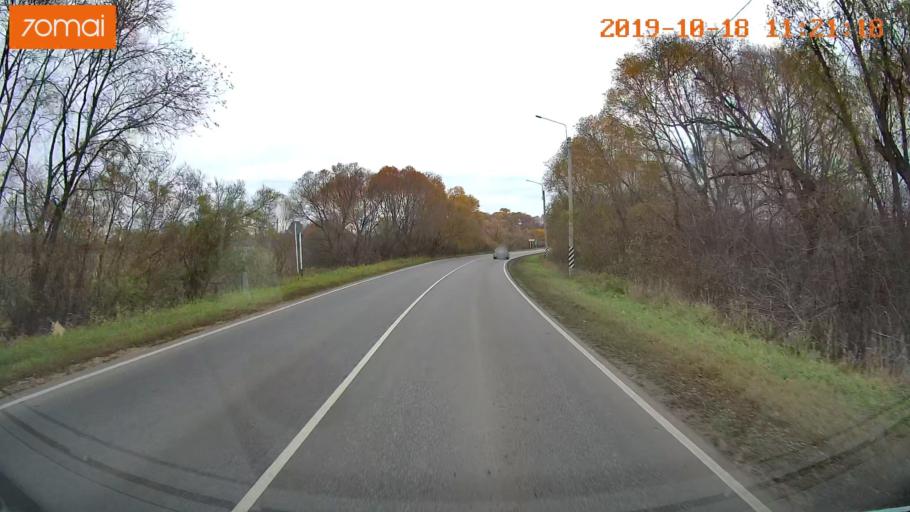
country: RU
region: Tula
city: Kimovsk
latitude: 54.0724
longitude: 38.5634
